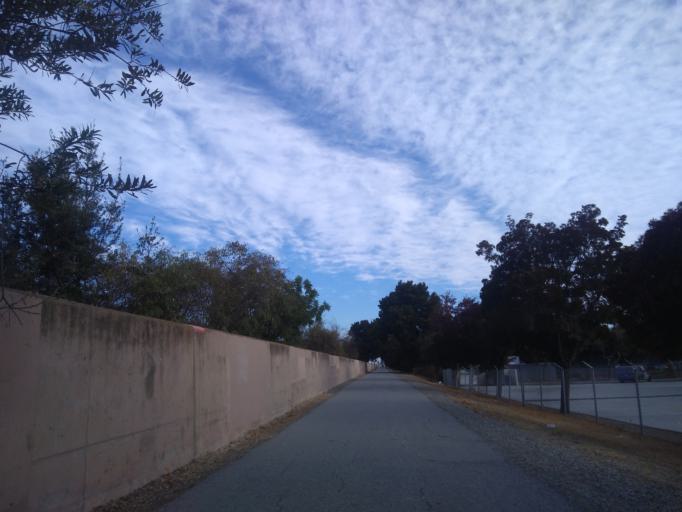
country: US
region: California
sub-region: Santa Clara County
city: Santa Clara
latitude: 37.4003
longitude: -121.9865
